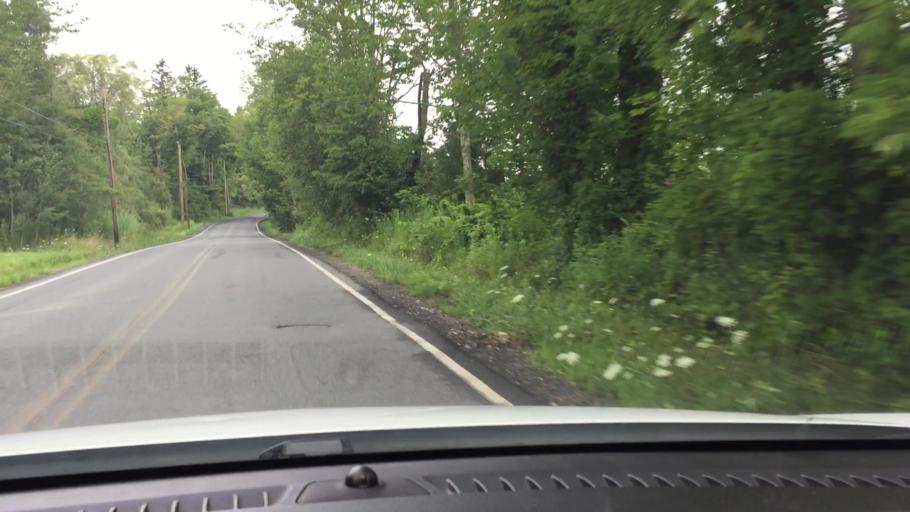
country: US
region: Massachusetts
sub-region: Berkshire County
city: Hinsdale
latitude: 42.4421
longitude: -73.1373
